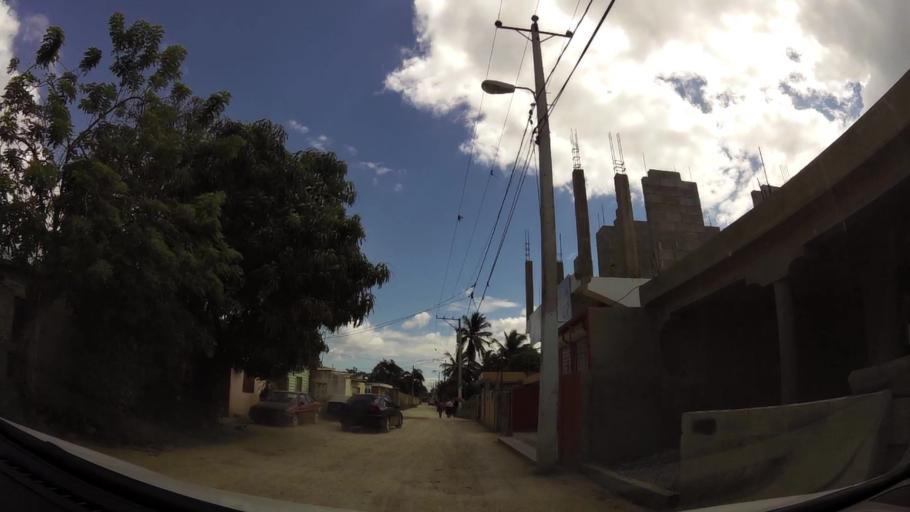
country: DO
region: Santo Domingo
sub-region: Santo Domingo
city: Boca Chica
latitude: 18.4534
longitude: -69.6325
